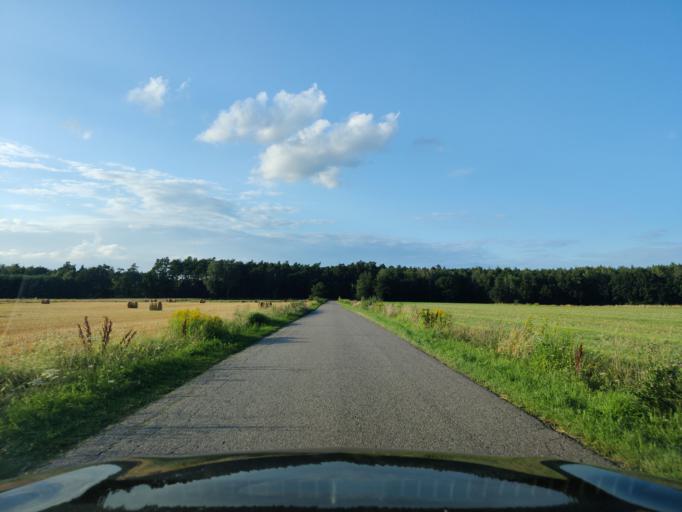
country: PL
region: Masovian Voivodeship
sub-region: Powiat pultuski
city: Obryte
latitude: 52.6759
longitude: 21.1876
